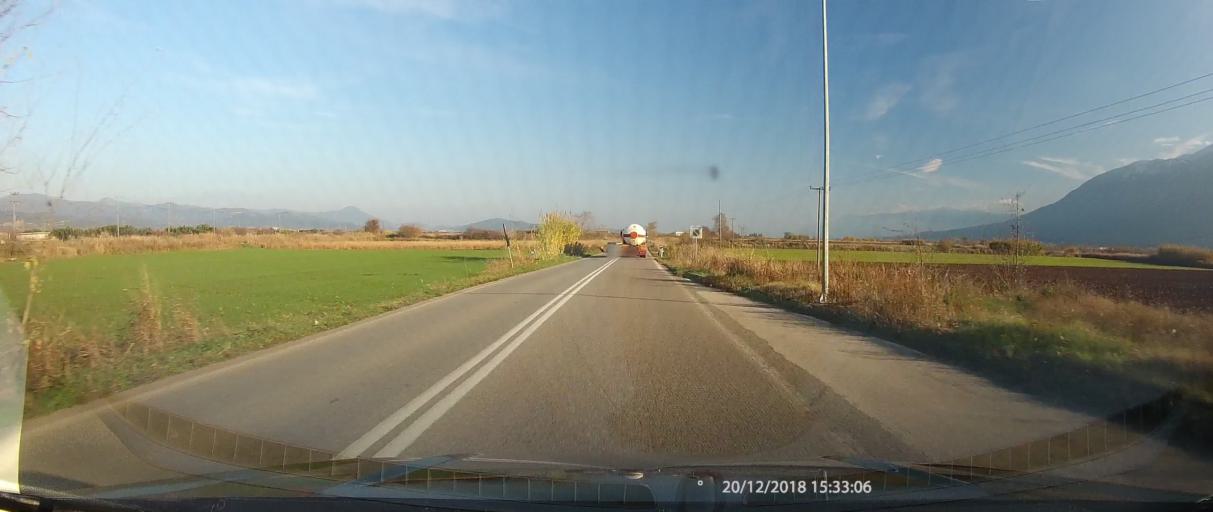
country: GR
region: Central Greece
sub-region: Nomos Fthiotidos
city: Lianokladhion
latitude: 38.9261
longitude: 22.2700
